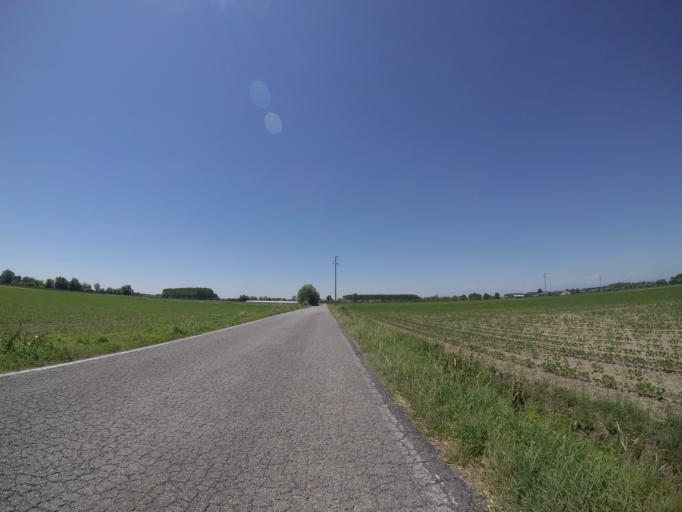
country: IT
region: Friuli Venezia Giulia
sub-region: Provincia di Udine
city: Teor
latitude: 45.8651
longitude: 13.0740
